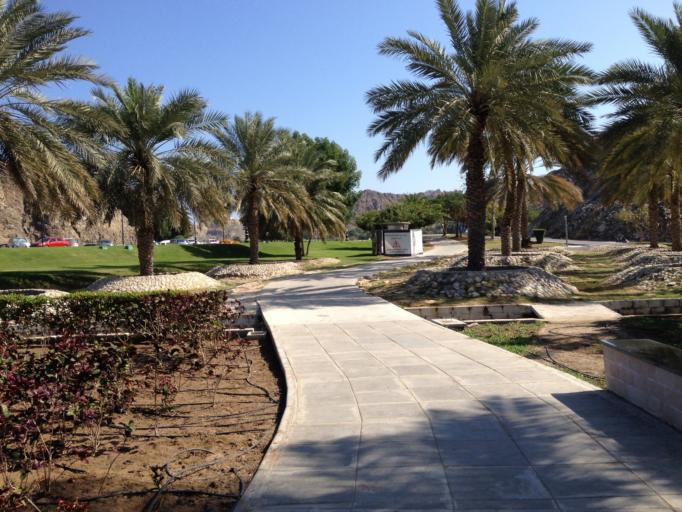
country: OM
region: Muhafazat Masqat
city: Muscat
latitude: 23.6219
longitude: 58.5723
